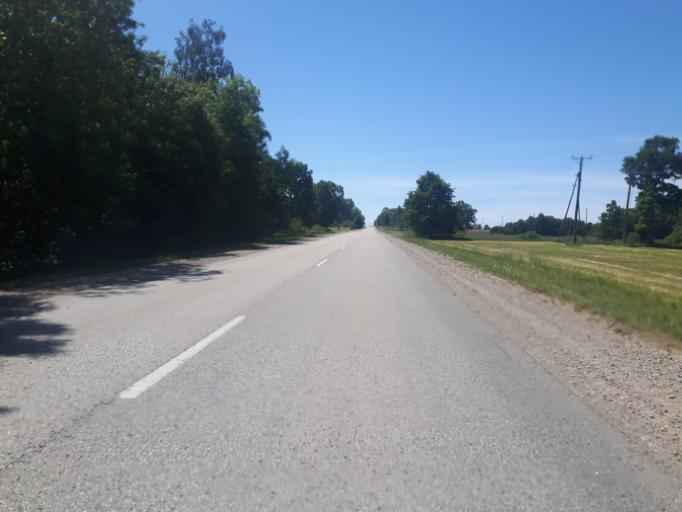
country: LV
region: Durbe
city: Liegi
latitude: 56.5928
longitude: 21.2739
